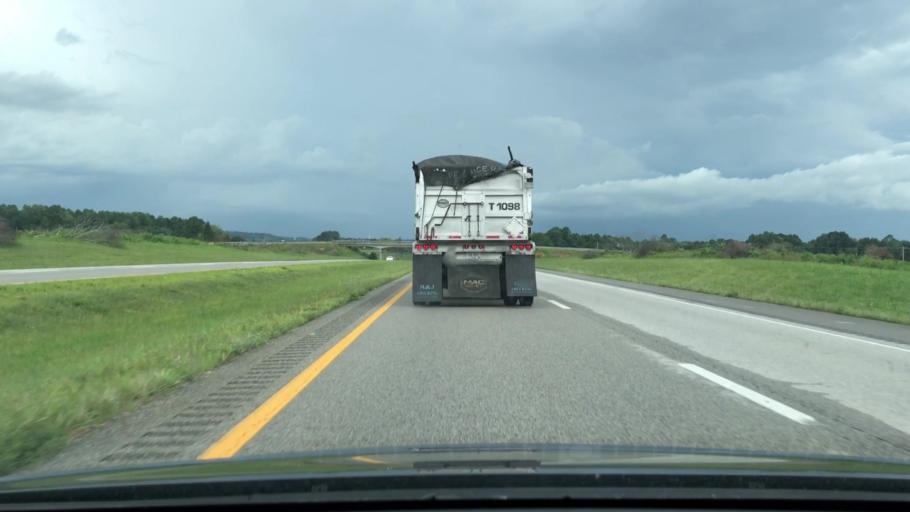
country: US
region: Kentucky
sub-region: Russell County
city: Russell Springs
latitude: 37.0865
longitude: -84.9277
